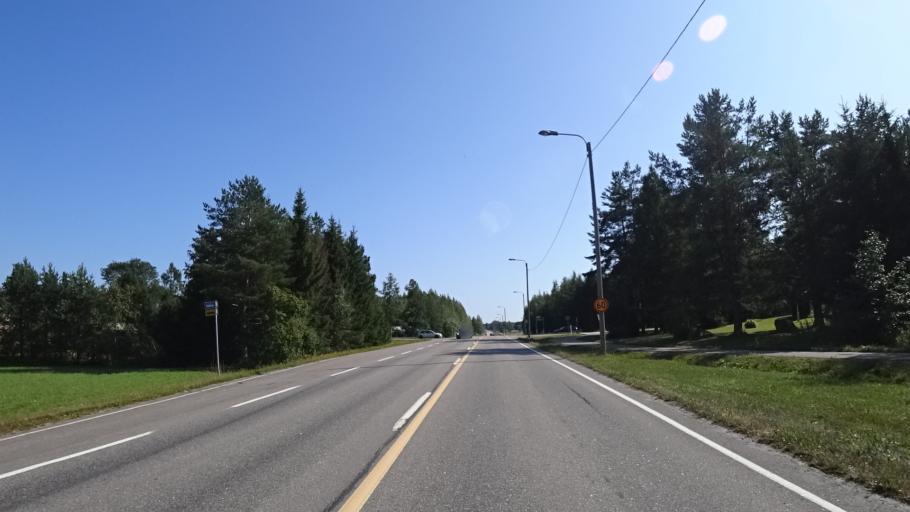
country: FI
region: Kymenlaakso
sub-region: Kotka-Hamina
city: Karhula
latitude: 60.5342
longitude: 26.9361
